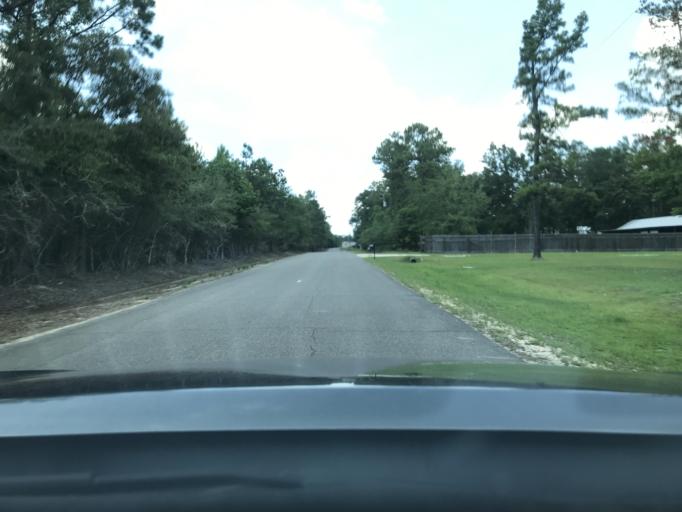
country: US
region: Louisiana
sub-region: Calcasieu Parish
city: Moss Bluff
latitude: 30.3321
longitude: -93.1308
